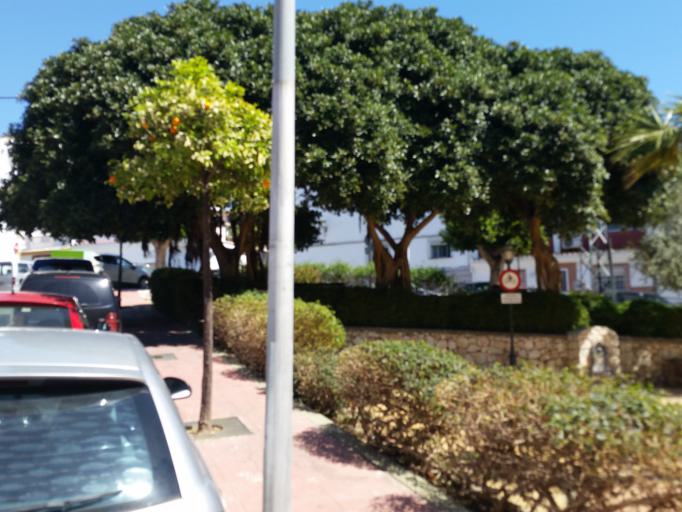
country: ES
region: Andalusia
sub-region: Provincia de Malaga
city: Benalmadena
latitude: 36.6011
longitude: -4.5355
